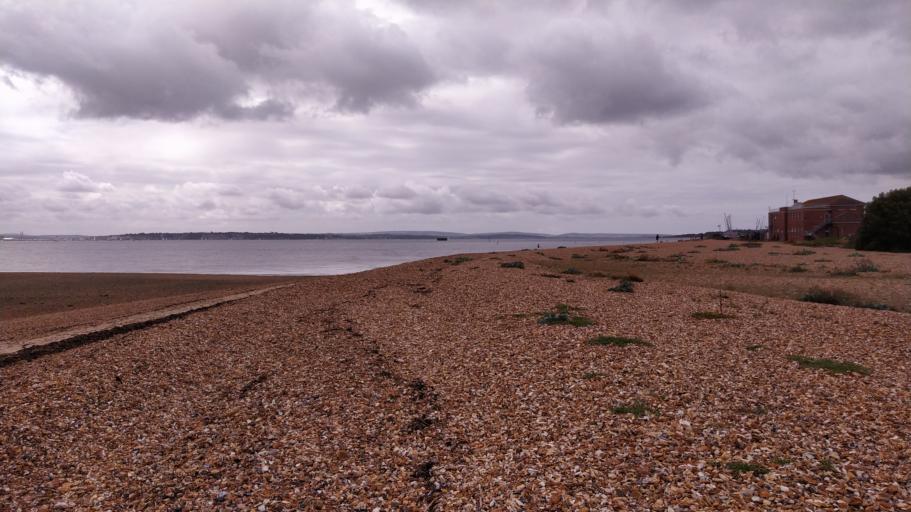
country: GB
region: England
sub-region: Hampshire
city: Hamble
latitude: 50.8157
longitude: -1.3072
